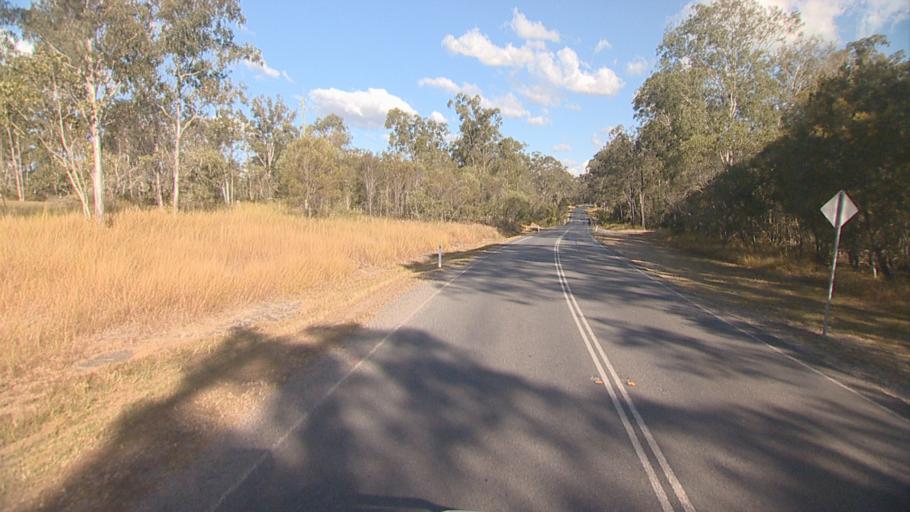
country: AU
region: Queensland
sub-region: Logan
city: North Maclean
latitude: -27.7551
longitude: 152.9878
